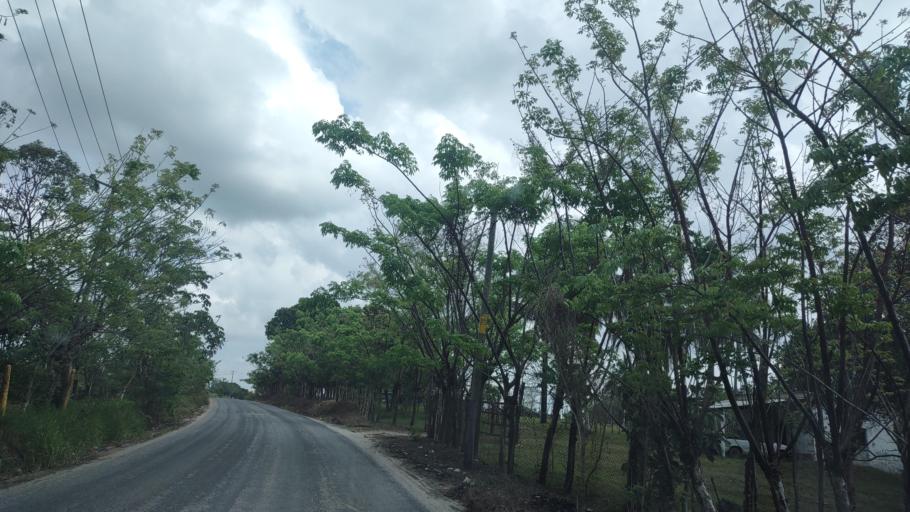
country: MX
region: Veracruz
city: Las Choapas
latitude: 17.9545
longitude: -94.1100
